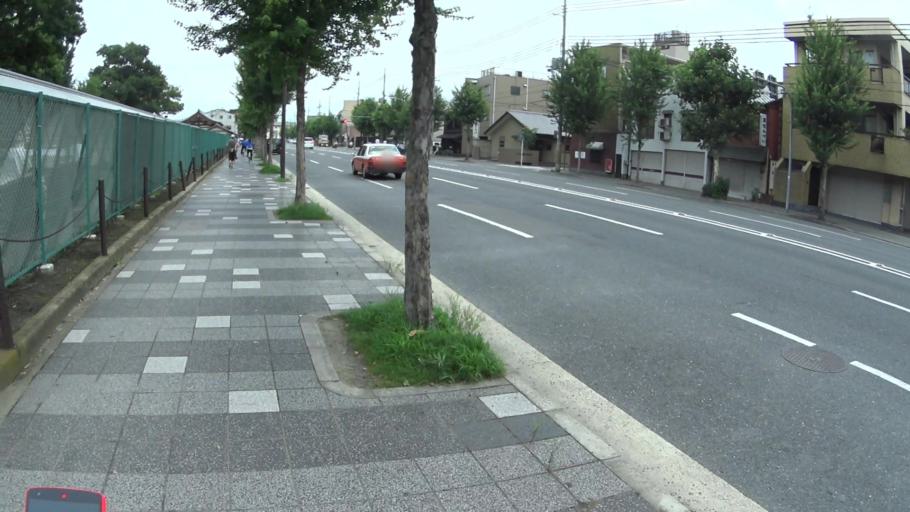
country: JP
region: Kyoto
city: Kyoto
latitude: 34.9807
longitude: 135.7491
